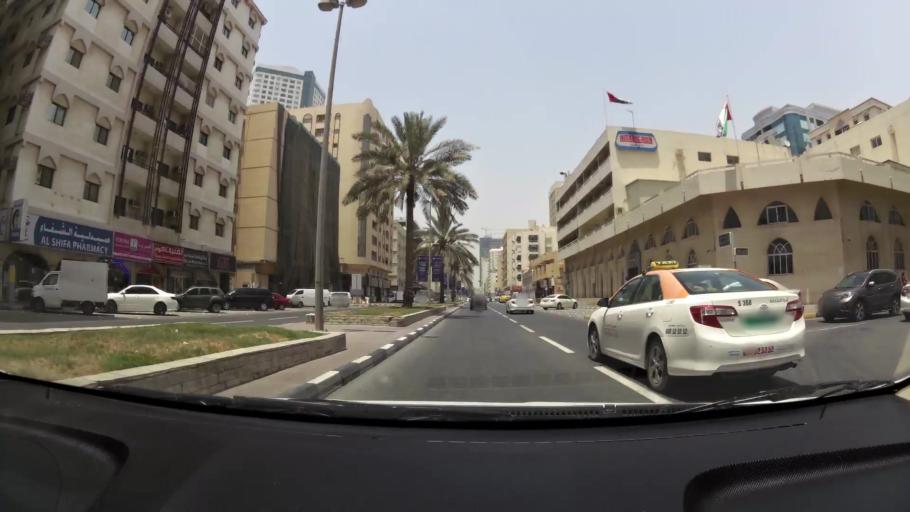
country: AE
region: Ash Shariqah
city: Sharjah
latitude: 25.3179
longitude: 55.3832
